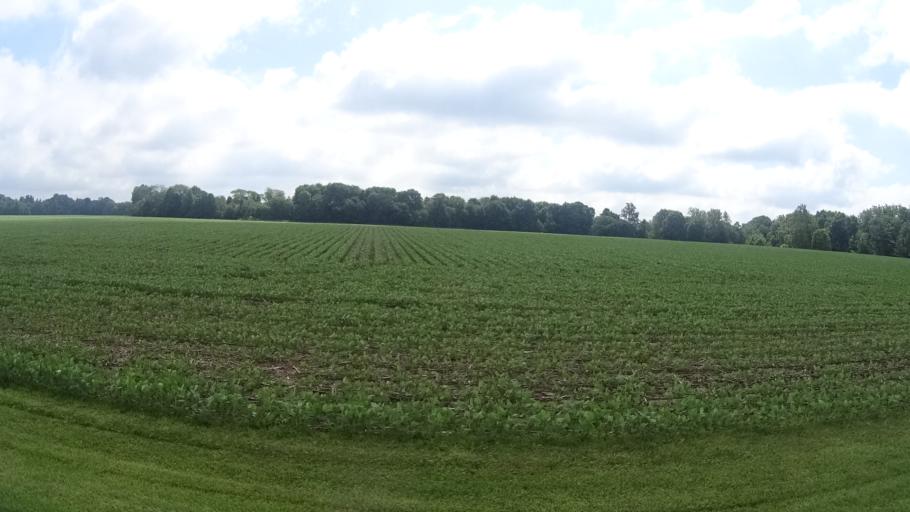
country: US
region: Ohio
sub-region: Huron County
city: Wakeman
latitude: 41.3051
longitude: -82.3873
